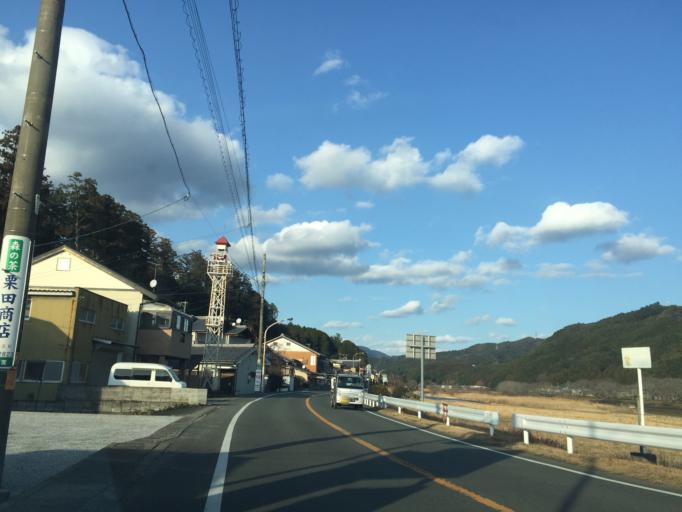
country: JP
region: Shizuoka
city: Mori
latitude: 34.8417
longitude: 137.9342
